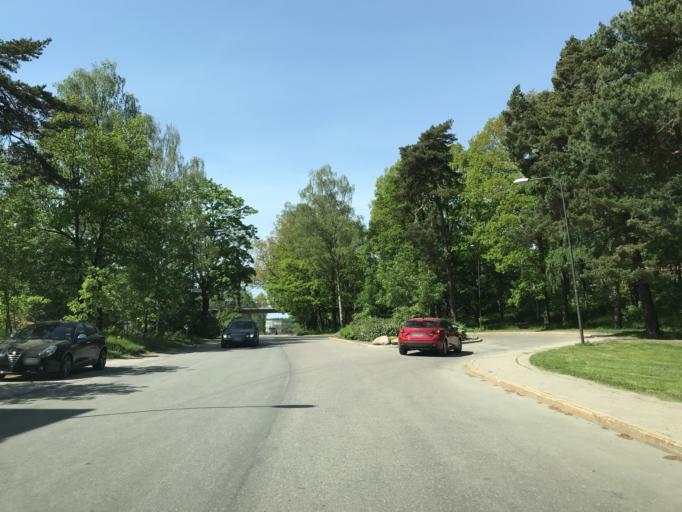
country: SE
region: Stockholm
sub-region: Stockholms Kommun
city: Stockholm
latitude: 59.3523
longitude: 18.0646
